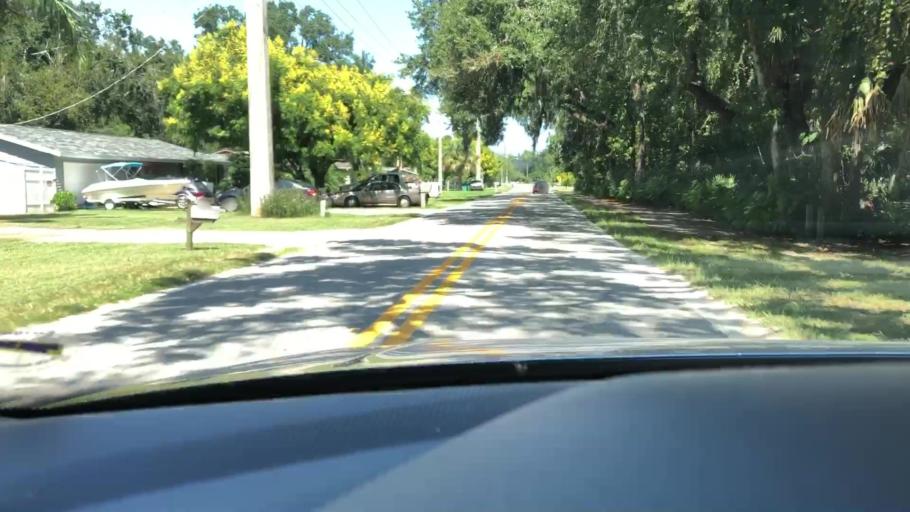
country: US
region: Florida
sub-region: Volusia County
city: Port Orange
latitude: 29.1272
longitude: -80.9930
